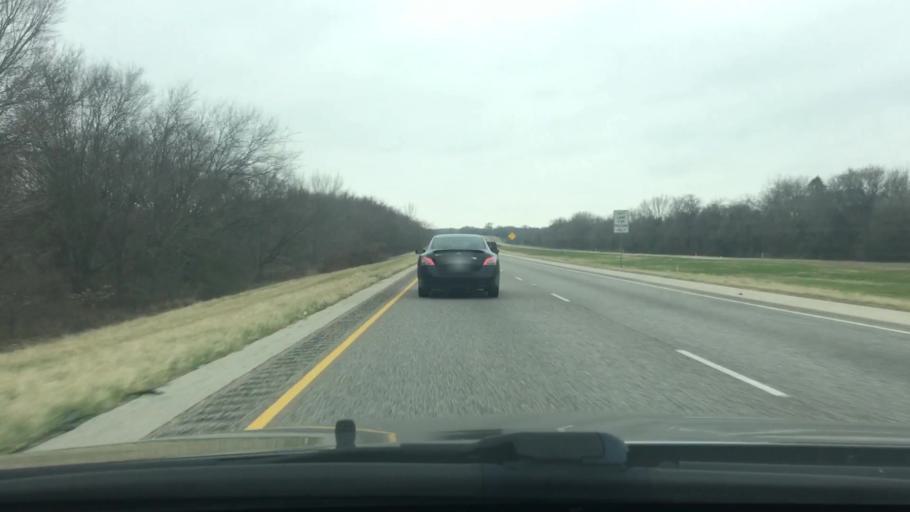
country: US
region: Texas
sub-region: Freestone County
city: Fairfield
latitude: 31.8004
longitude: -96.2585
